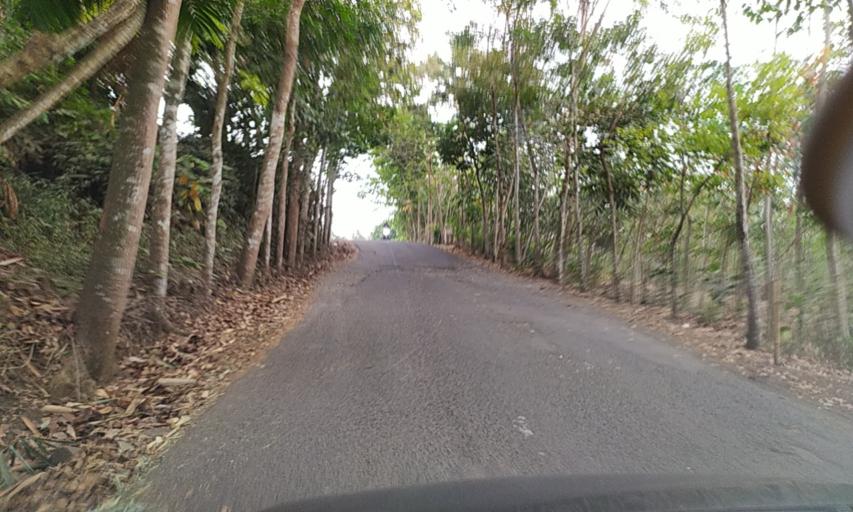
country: ID
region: Central Java
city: Ciwalen
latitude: -7.2867
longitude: 108.6022
